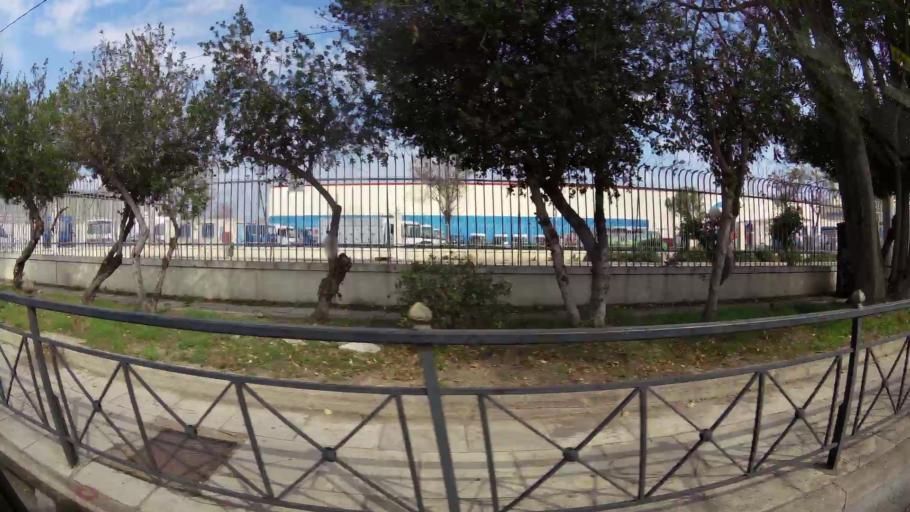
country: GR
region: Attica
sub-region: Nomarchia Athinas
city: Athens
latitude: 37.9847
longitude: 23.7024
